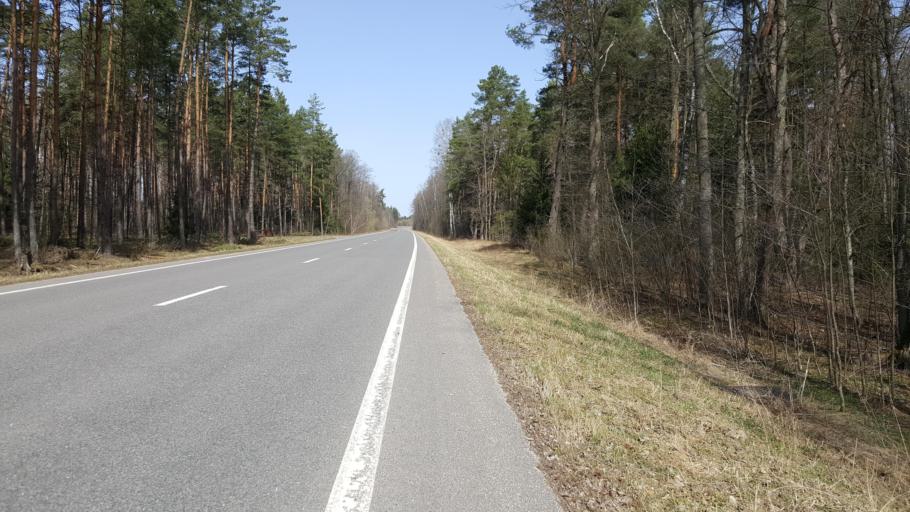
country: BY
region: Brest
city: Kamyanyuki
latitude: 52.5383
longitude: 23.6545
